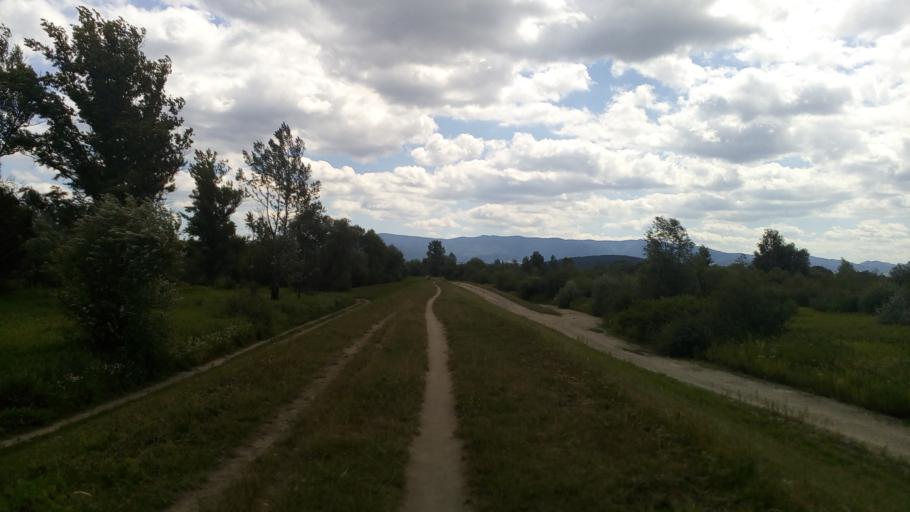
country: PL
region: Lesser Poland Voivodeship
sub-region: Powiat nowosadecki
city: Stary Sacz
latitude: 49.5937
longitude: 20.6553
